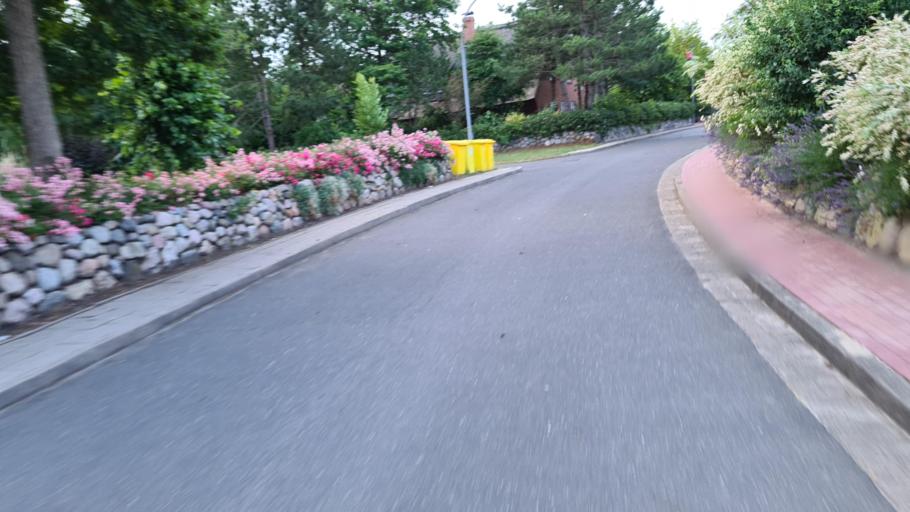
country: DE
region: Schleswig-Holstein
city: Sankt Peter-Ording
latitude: 54.2939
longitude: 8.6564
